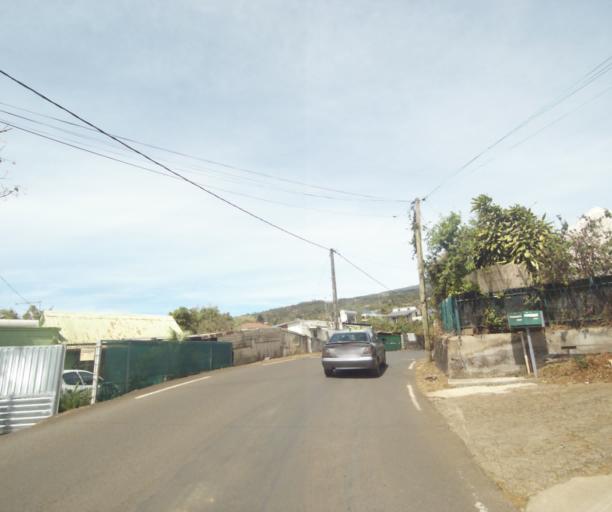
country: RE
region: Reunion
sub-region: Reunion
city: Saint-Paul
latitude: -21.0377
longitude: 55.3068
